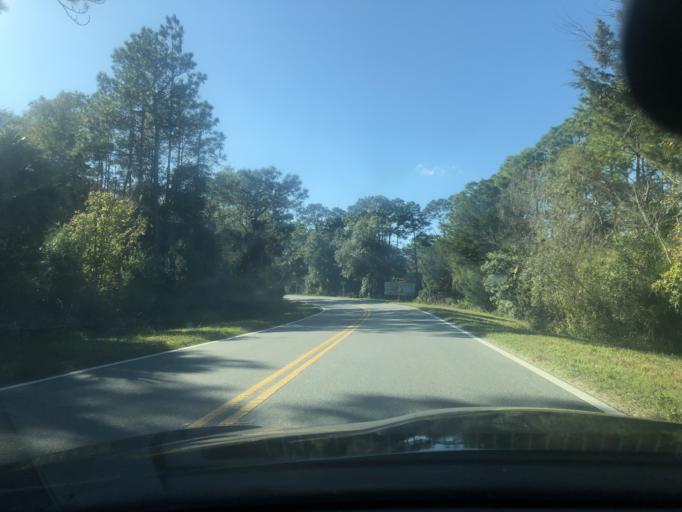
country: US
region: Florida
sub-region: Citrus County
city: Homosassa Springs
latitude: 28.8184
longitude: -82.5588
